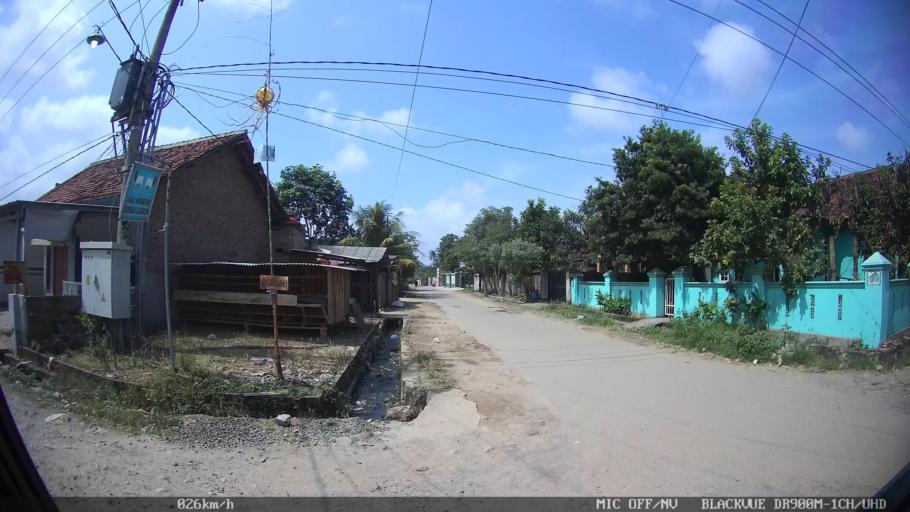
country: ID
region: Lampung
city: Kedaton
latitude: -5.3415
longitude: 105.2847
